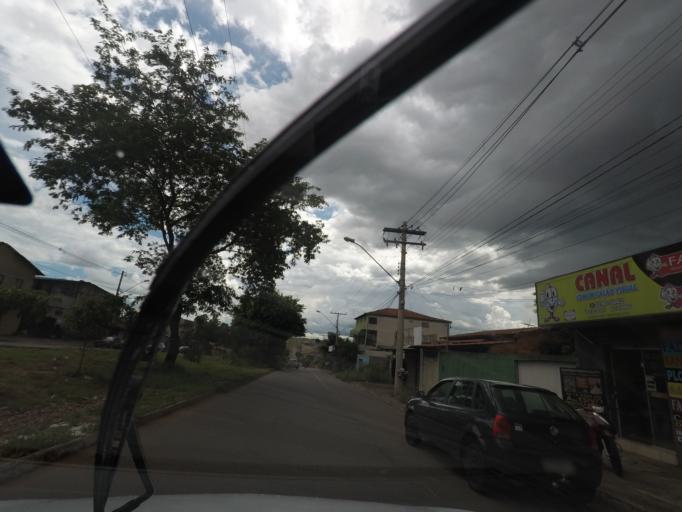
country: BR
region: Goias
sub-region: Goiania
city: Goiania
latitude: -16.7316
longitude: -49.3528
